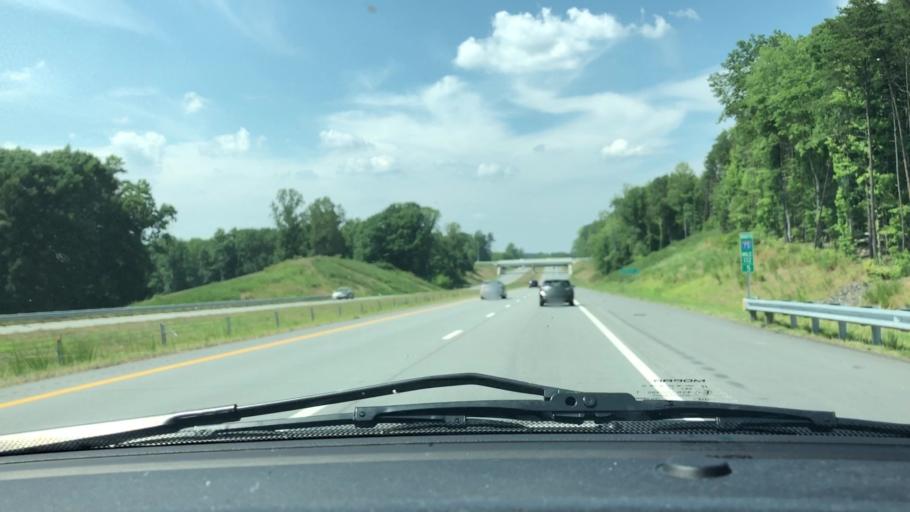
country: US
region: North Carolina
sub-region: Guilford County
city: Oak Ridge
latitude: 36.1476
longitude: -79.9587
